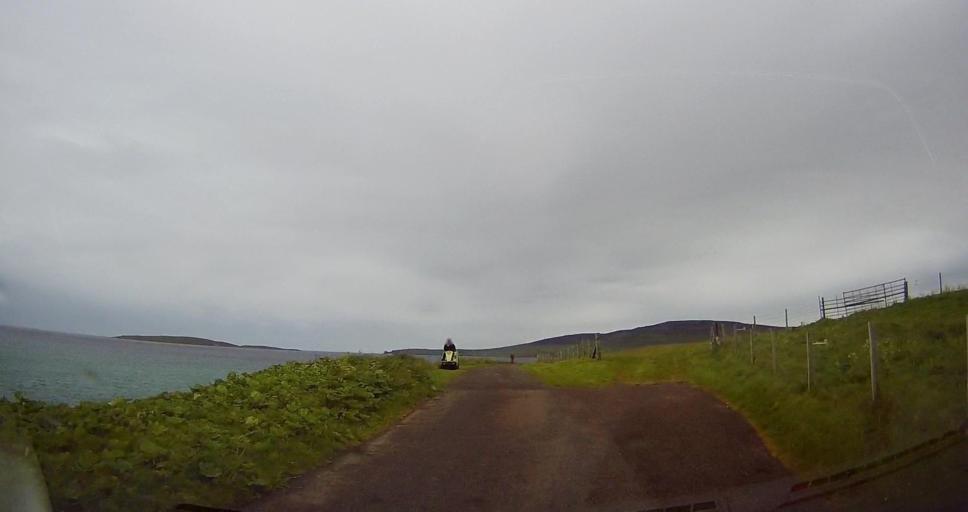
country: GB
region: Scotland
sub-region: Orkney Islands
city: Orkney
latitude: 59.1213
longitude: -3.0851
